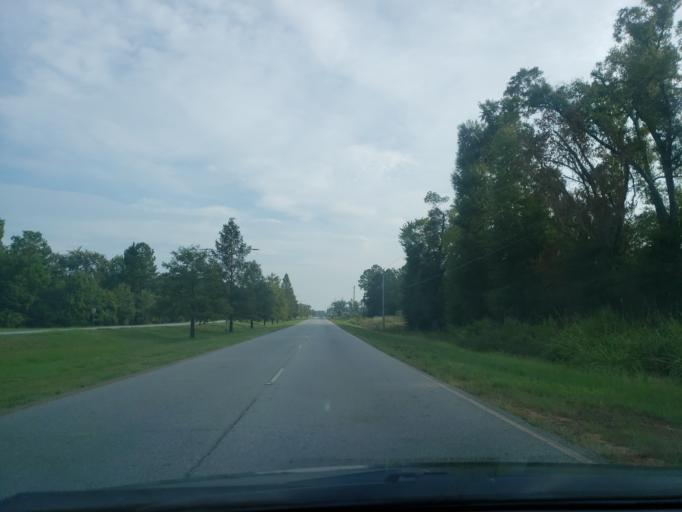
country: US
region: Georgia
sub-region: Dougherty County
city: Albany
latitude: 31.5800
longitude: -84.2193
